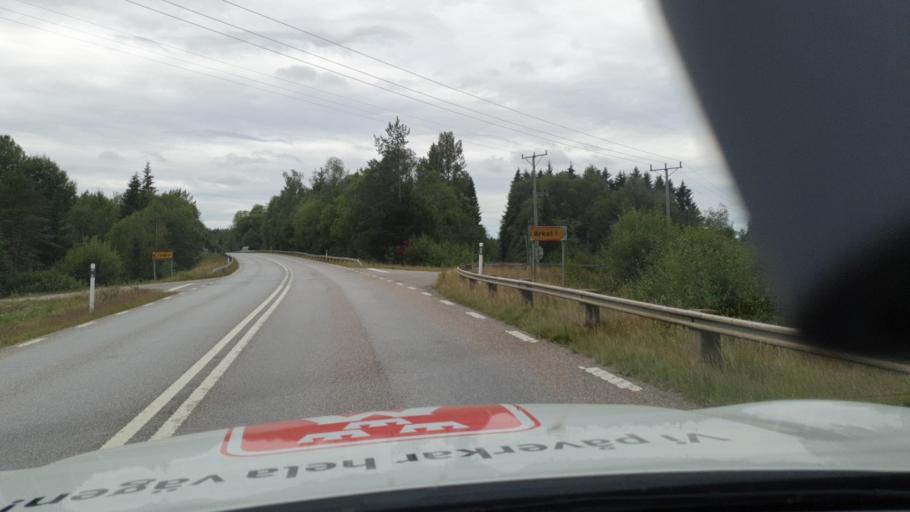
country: SE
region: Vaestra Goetaland
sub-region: Bengtsfors Kommun
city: Dals Langed
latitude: 58.7680
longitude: 12.2260
